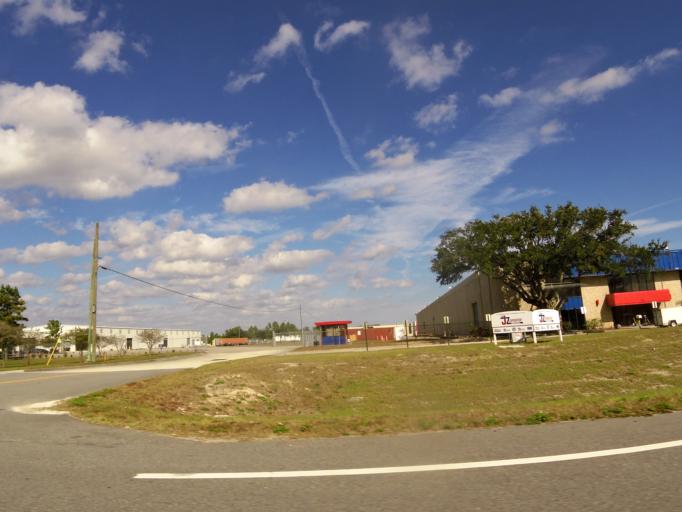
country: US
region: Florida
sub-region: Duval County
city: Jacksonville
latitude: 30.4164
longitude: -81.6303
